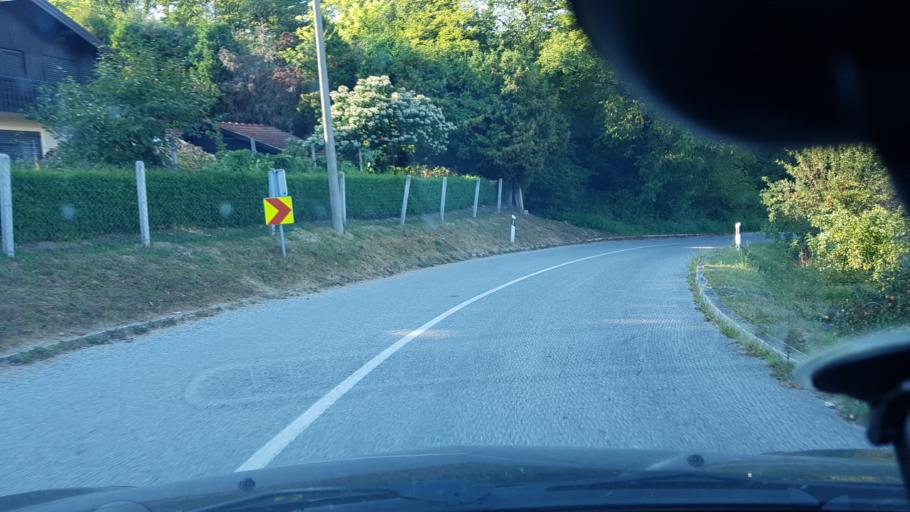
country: SI
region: Bistrica ob Sotli
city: Bistrica ob Sotli
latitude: 46.0496
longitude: 15.7497
